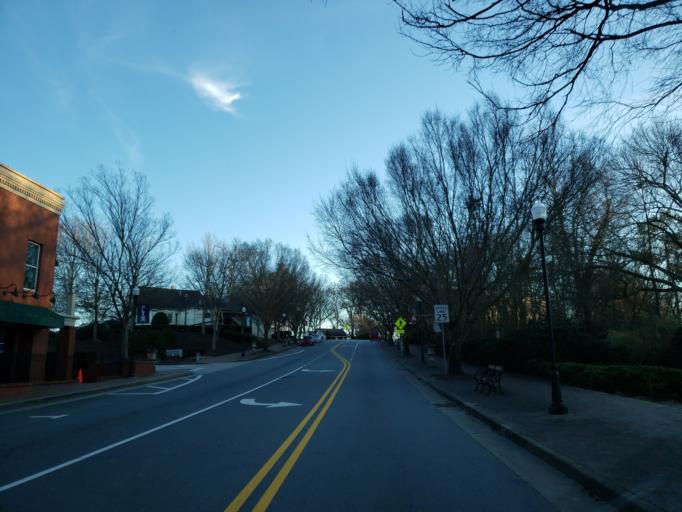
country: US
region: Georgia
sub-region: Fulton County
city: Alpharetta
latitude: 34.0754
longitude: -84.2966
